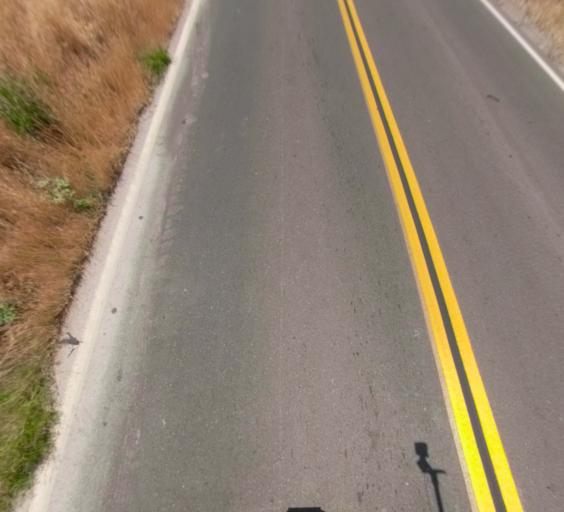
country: US
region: California
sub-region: Madera County
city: Madera Acres
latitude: 37.0348
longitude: -120.0290
